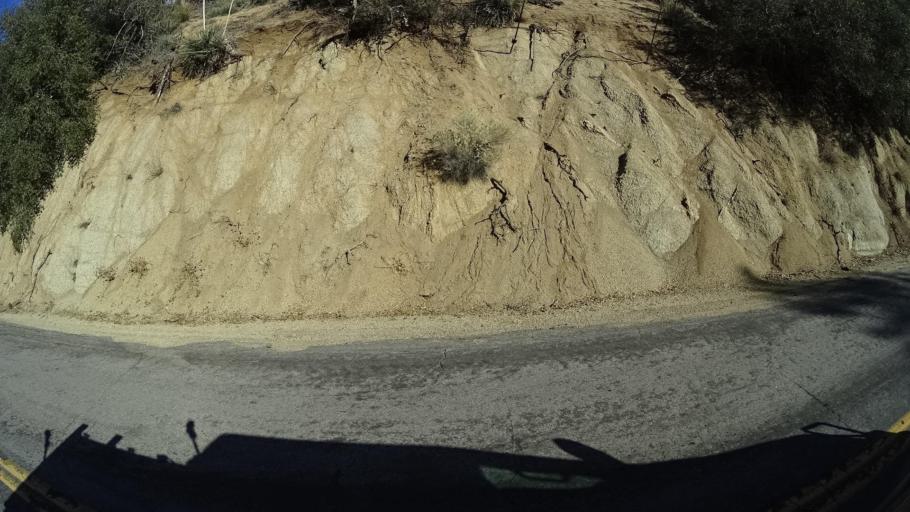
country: US
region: California
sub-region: Kern County
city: Bodfish
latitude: 35.4699
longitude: -118.5303
